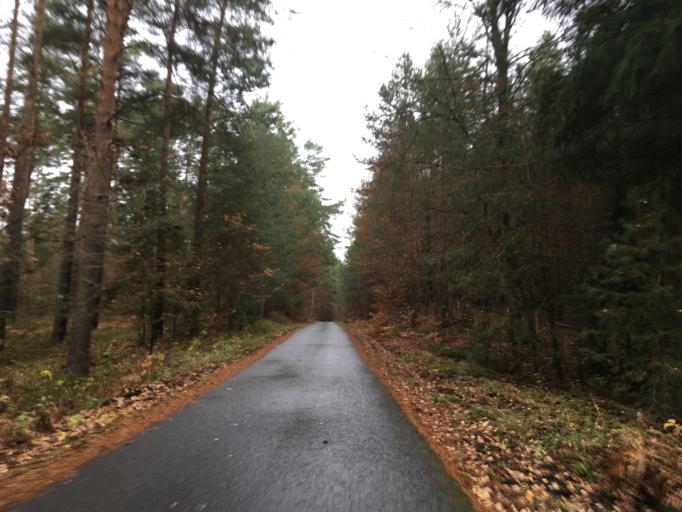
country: DE
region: Brandenburg
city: Jamlitz
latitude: 52.0437
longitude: 14.4773
